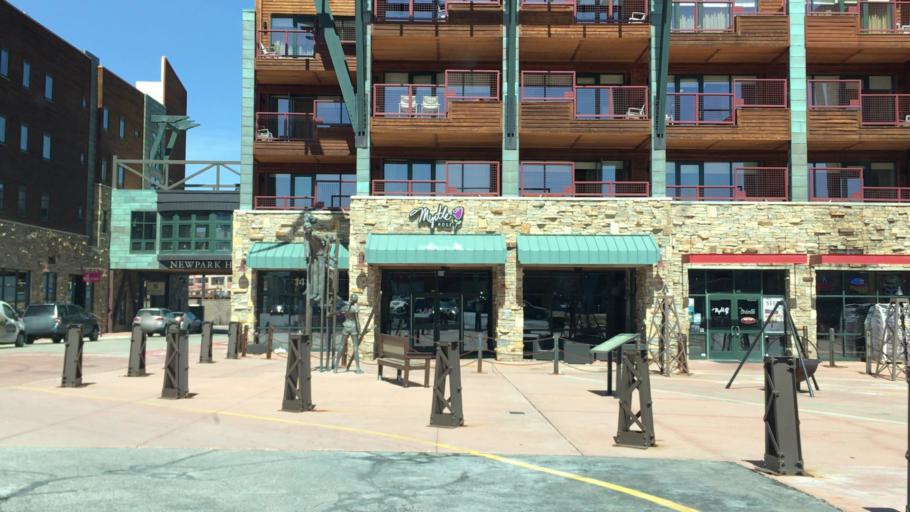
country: US
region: Utah
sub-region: Summit County
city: Snyderville
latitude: 40.7216
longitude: -111.5386
